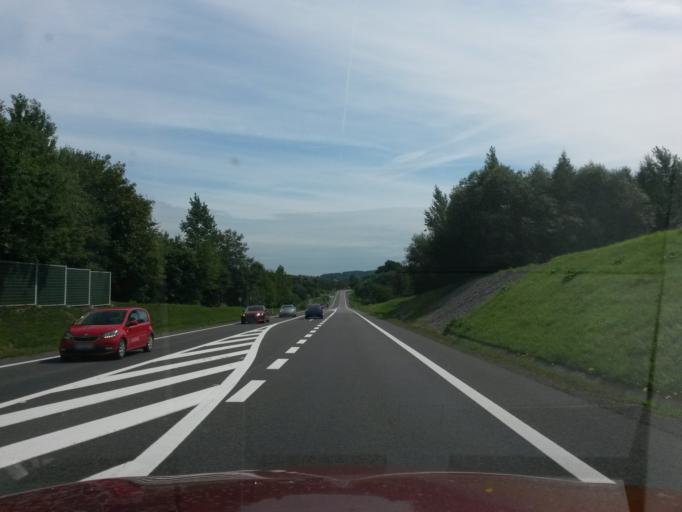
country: PL
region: Lesser Poland Voivodeship
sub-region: Powiat bochenski
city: Stanislawice
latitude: 49.9633
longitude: 20.3484
